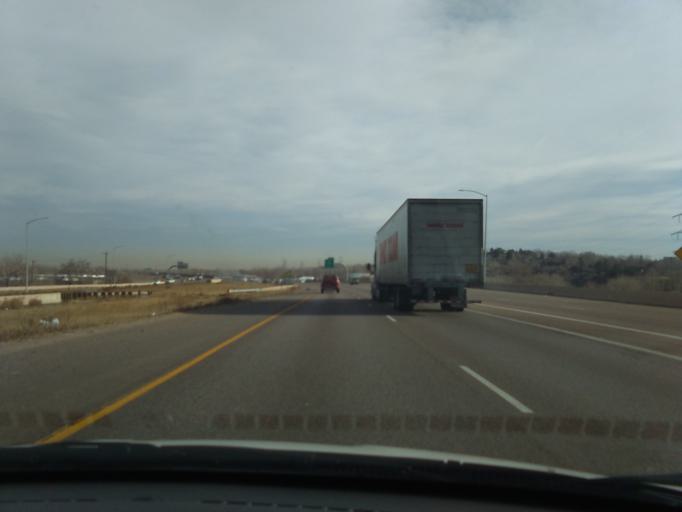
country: US
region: Colorado
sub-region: Jefferson County
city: Wheat Ridge
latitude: 39.7871
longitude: -105.0712
